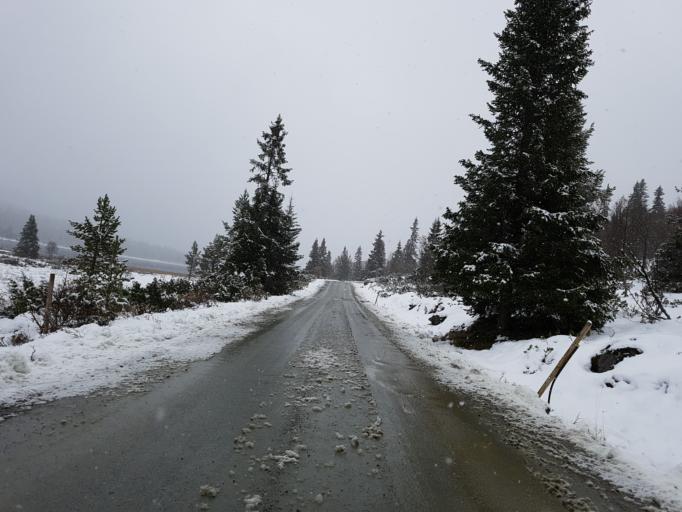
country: NO
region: Oppland
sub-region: Sel
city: Otta
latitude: 61.7943
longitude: 9.7153
